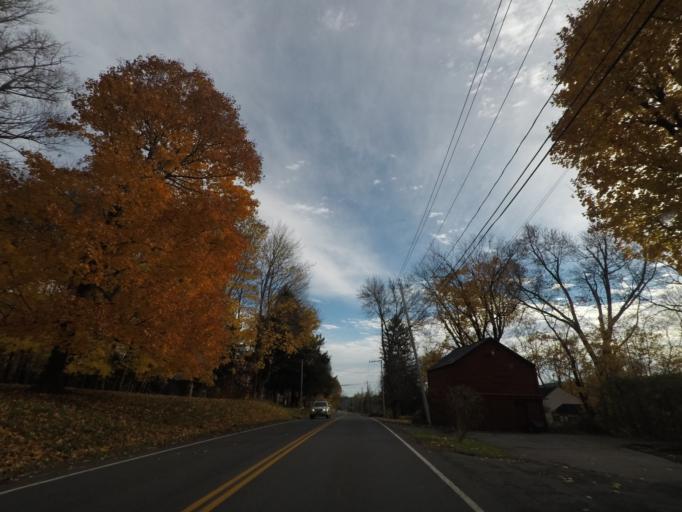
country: US
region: New York
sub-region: Albany County
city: Voorheesville
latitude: 42.6298
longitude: -73.9075
